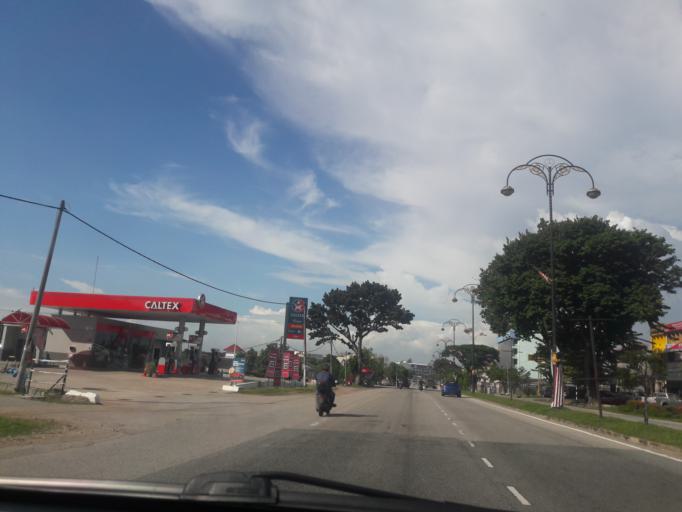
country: MY
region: Kedah
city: Sungai Petani
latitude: 5.6300
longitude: 100.4810
